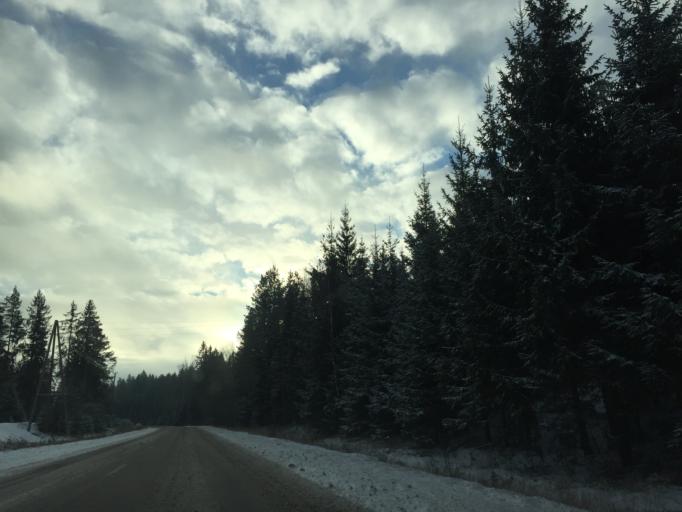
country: LV
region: Amatas Novads
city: Drabesi
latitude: 57.2231
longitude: 25.2844
